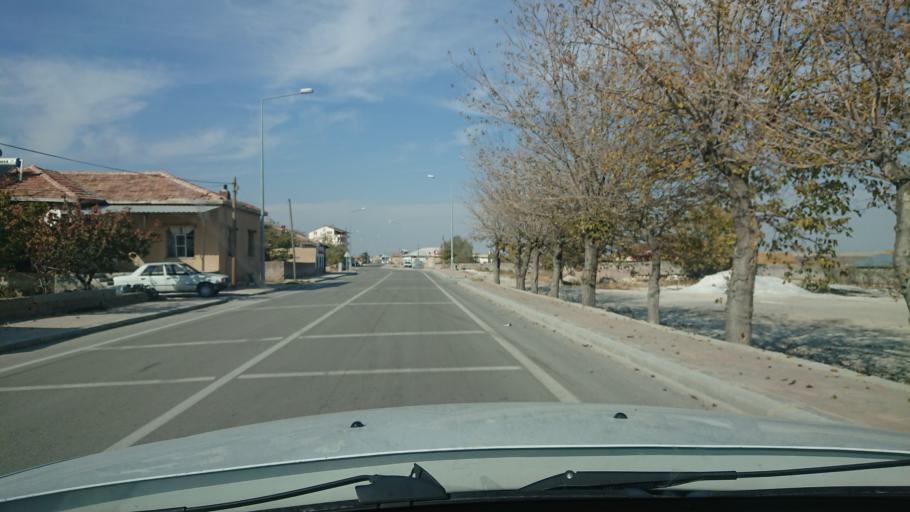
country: TR
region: Aksaray
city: Sultanhani
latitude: 38.2613
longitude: 33.4443
